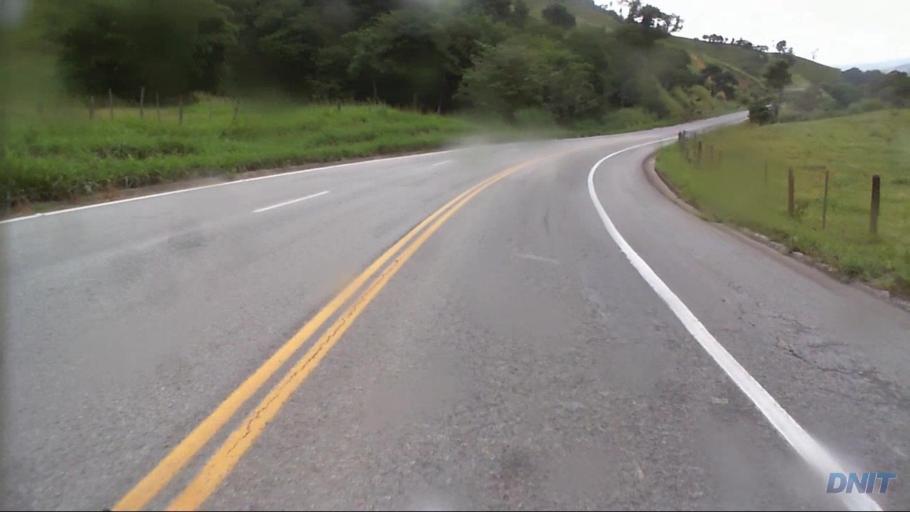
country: BR
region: Minas Gerais
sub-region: Nova Era
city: Nova Era
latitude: -19.7127
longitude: -43.0002
